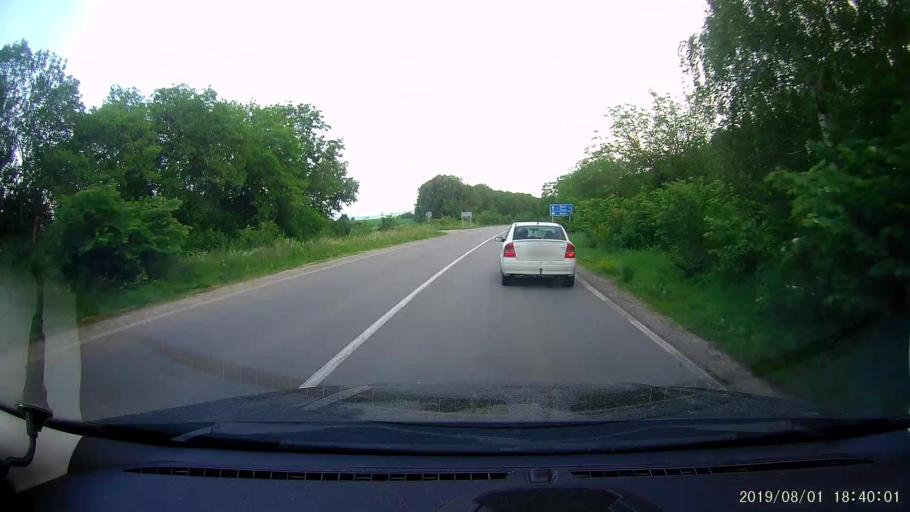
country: BG
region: Shumen
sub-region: Obshtina Khitrino
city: Gara Khitrino
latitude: 43.3745
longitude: 26.9201
